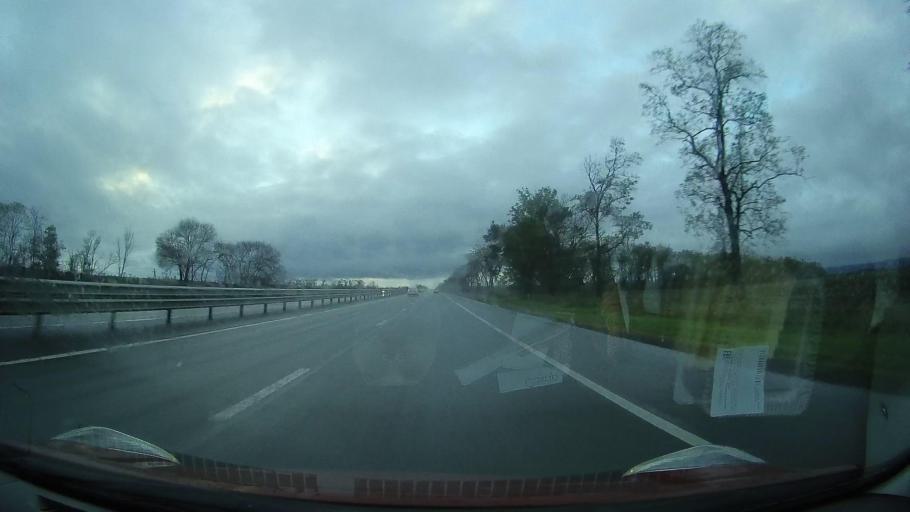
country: RU
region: Stavropol'skiy
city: Zavetnoye
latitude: 44.7877
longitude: 41.5089
